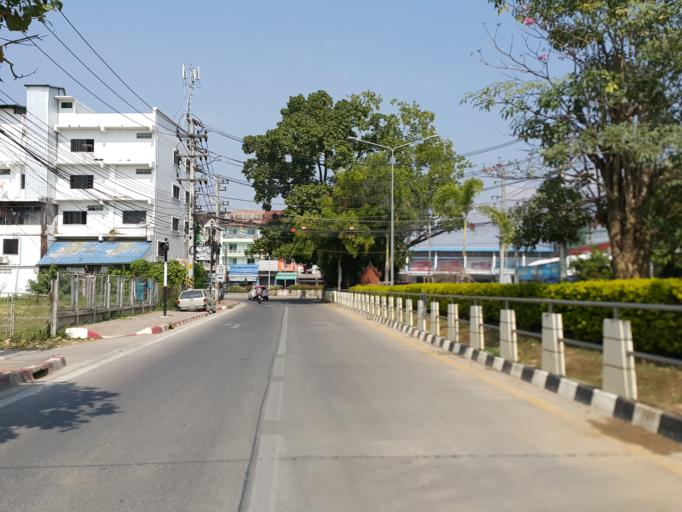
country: TH
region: Chiang Mai
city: Chiang Mai
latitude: 18.8100
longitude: 98.9953
